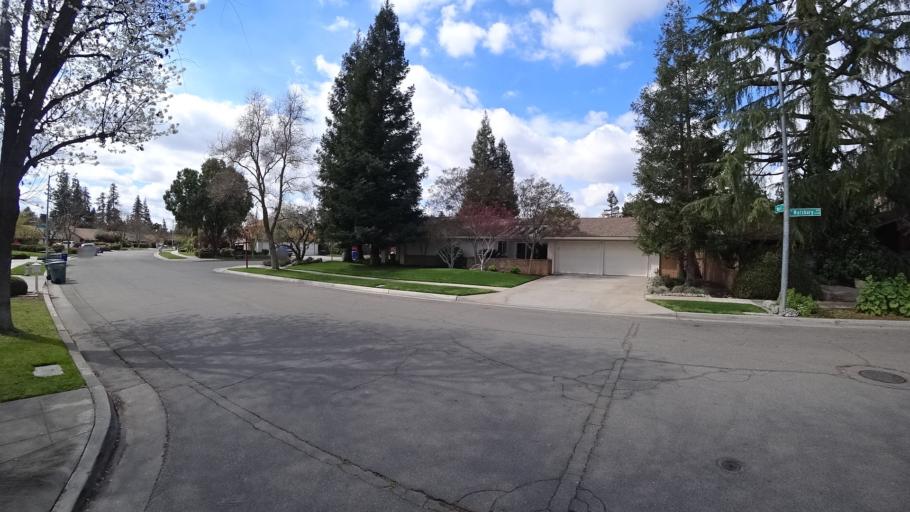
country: US
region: California
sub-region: Fresno County
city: Fresno
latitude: 36.8360
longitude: -119.8545
